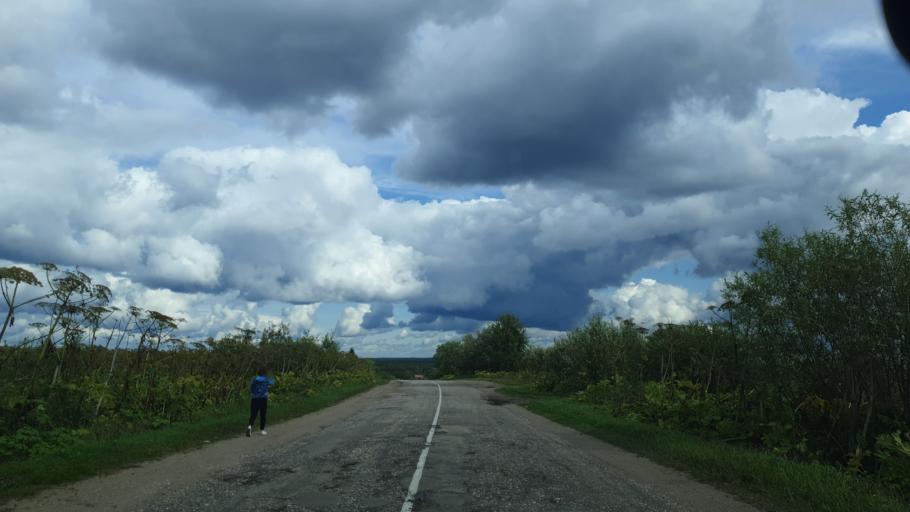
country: RU
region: Komi Republic
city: Aykino
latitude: 61.9574
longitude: 50.1846
